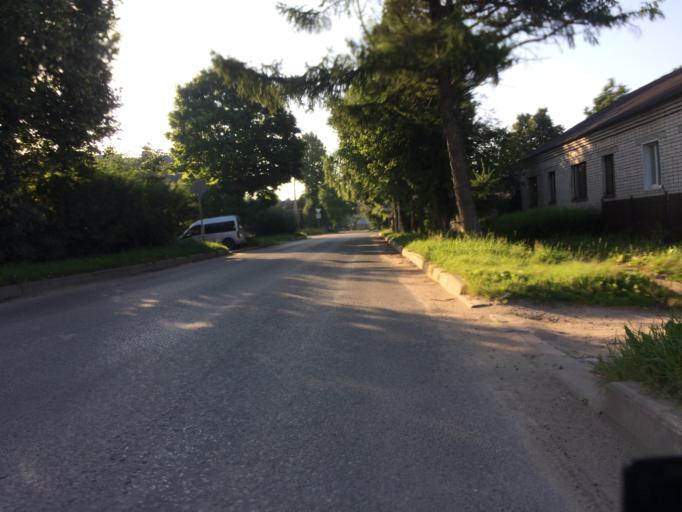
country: RU
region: Mariy-El
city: Yoshkar-Ola
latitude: 56.6514
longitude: 47.9019
